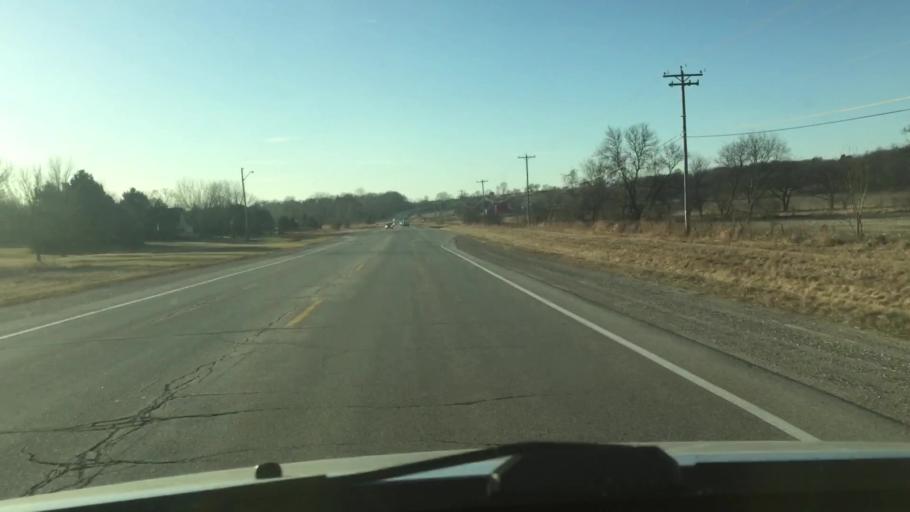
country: US
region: Wisconsin
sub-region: Waukesha County
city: Pewaukee
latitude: 43.1123
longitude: -88.2514
